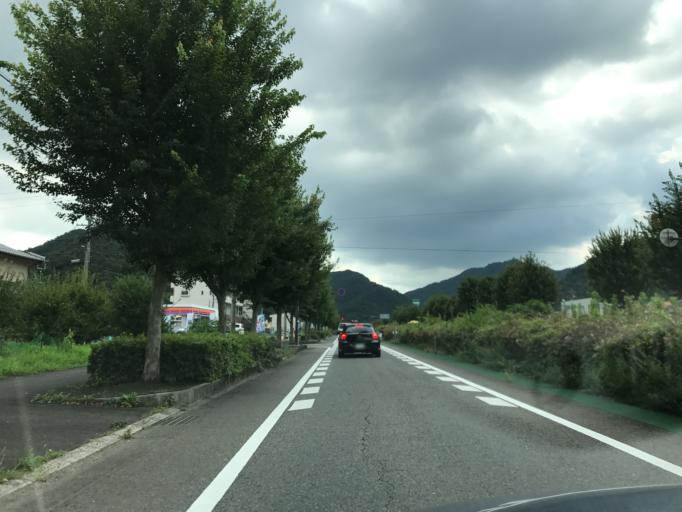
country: JP
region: Gifu
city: Gifu-shi
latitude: 35.4293
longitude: 136.8094
